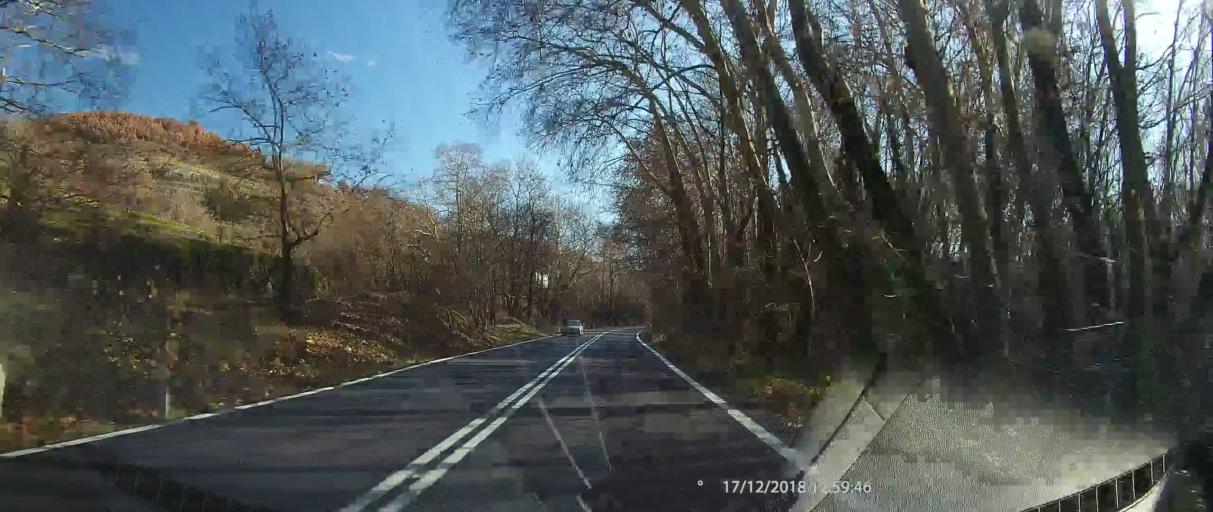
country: GR
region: Thessaly
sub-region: Trikala
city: Kastraki
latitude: 39.7345
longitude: 21.5600
